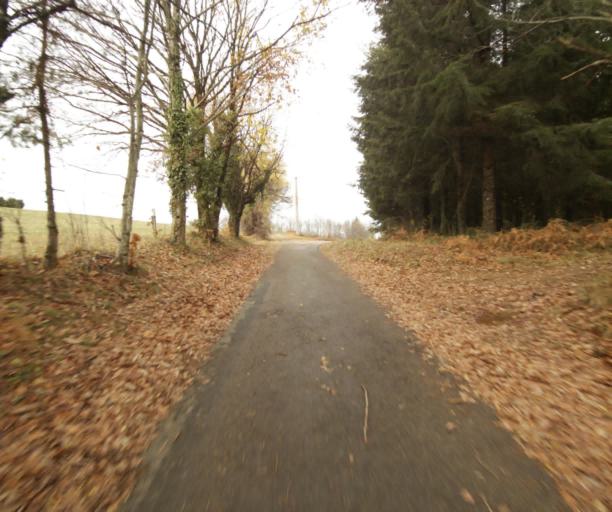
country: FR
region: Limousin
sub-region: Departement de la Correze
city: Sainte-Fortunade
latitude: 45.1926
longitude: 1.7670
